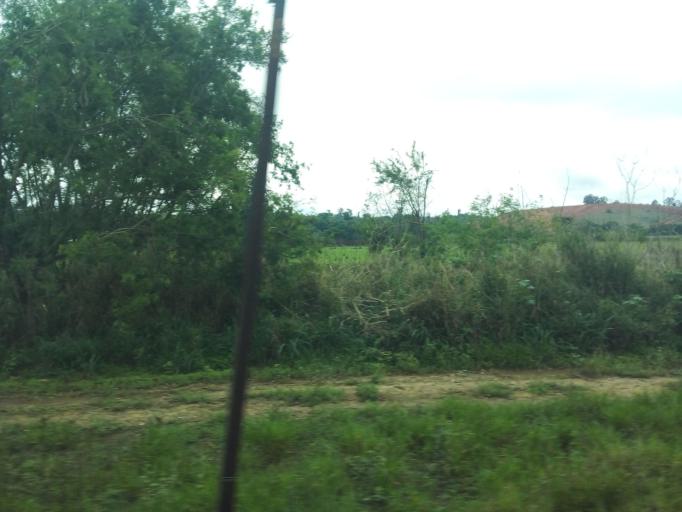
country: BR
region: Minas Gerais
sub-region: Ipatinga
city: Ipatinga
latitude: -19.4734
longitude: -42.4841
